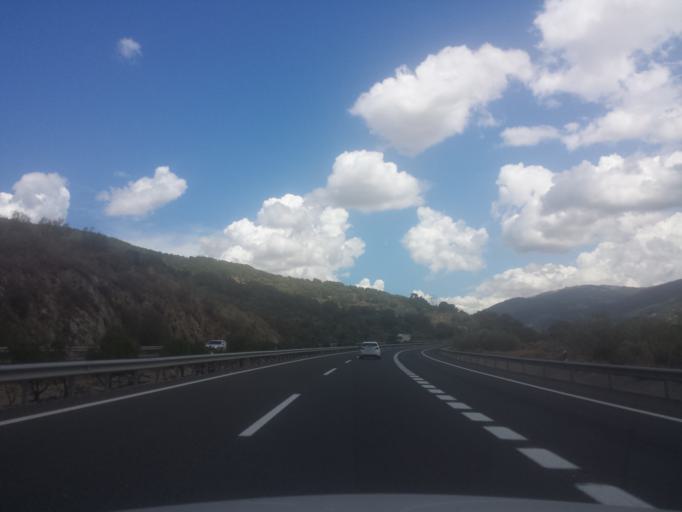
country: ES
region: Extremadura
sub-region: Provincia de Caceres
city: Hervas
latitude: 40.2917
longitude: -5.8981
